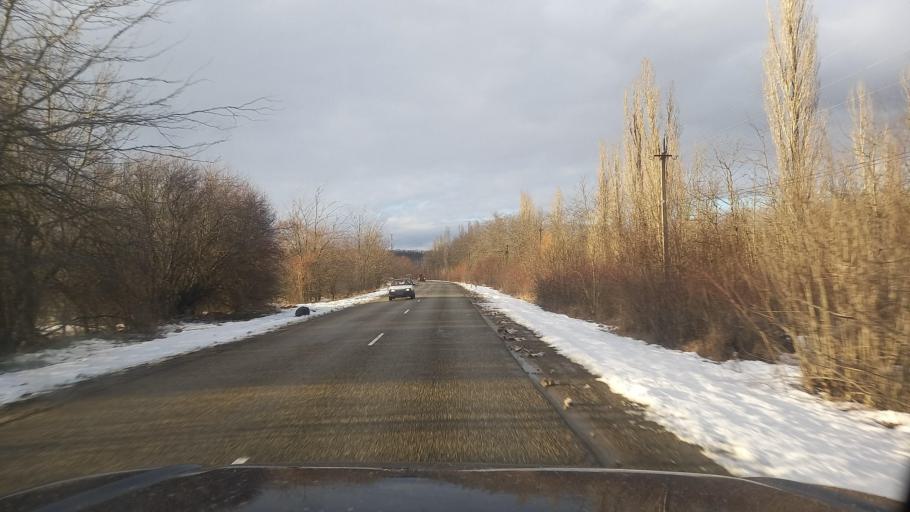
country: RU
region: Krasnodarskiy
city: Smolenskaya
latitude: 44.7792
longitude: 38.8109
